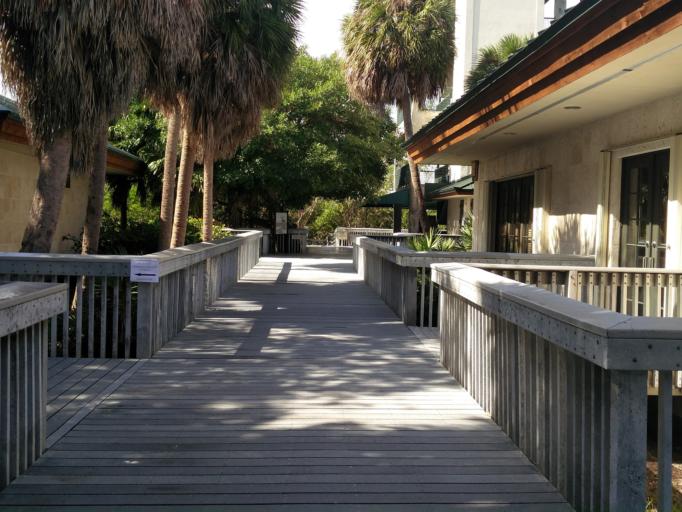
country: US
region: Florida
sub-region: Broward County
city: Dania Beach
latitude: 26.0385
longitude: -80.1197
